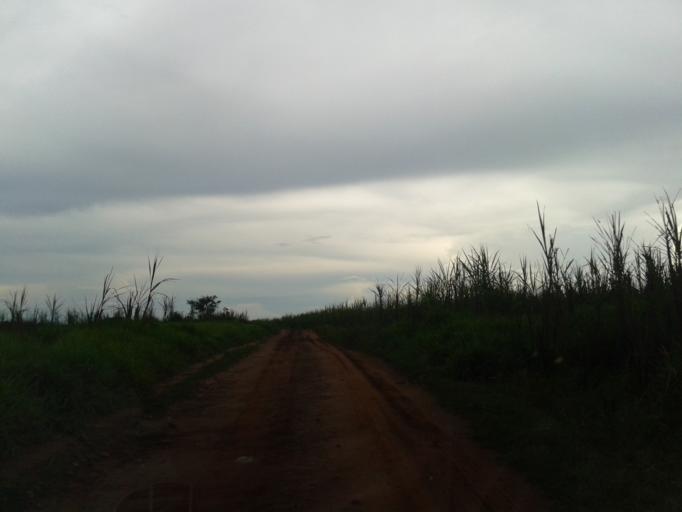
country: BR
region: Minas Gerais
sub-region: Santa Vitoria
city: Santa Vitoria
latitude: -19.1666
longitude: -50.5466
